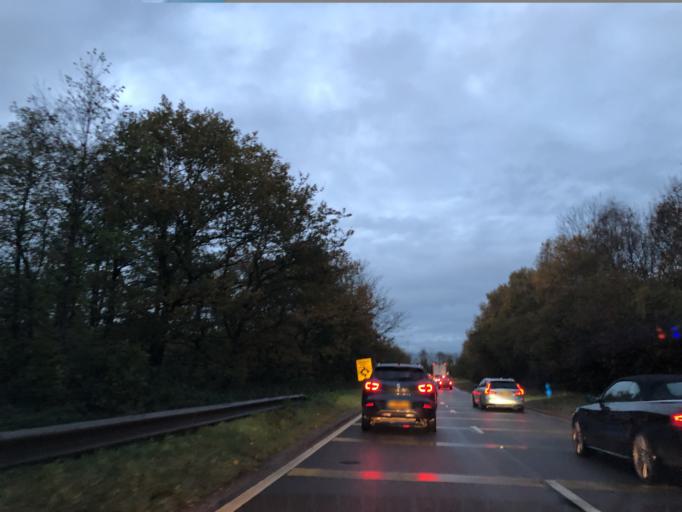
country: GB
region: England
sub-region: Solihull
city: Chelmsley Wood
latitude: 52.4735
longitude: -1.7069
